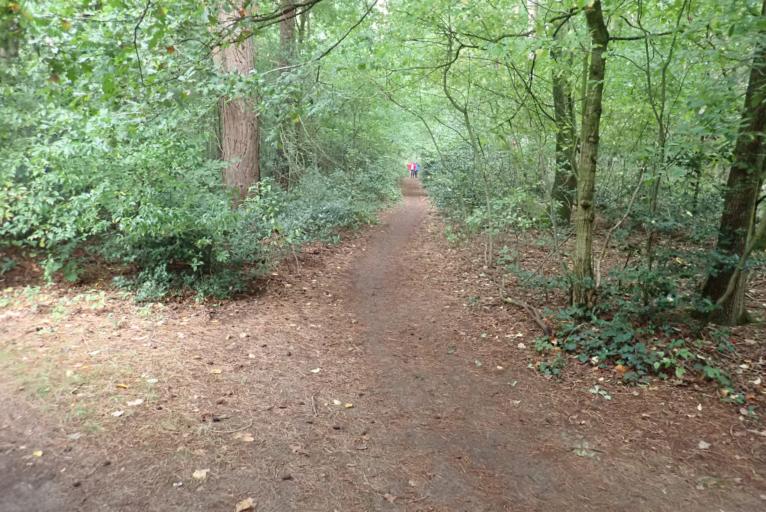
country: BE
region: Flanders
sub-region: Provincie Antwerpen
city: Lille
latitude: 51.2208
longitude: 4.8319
